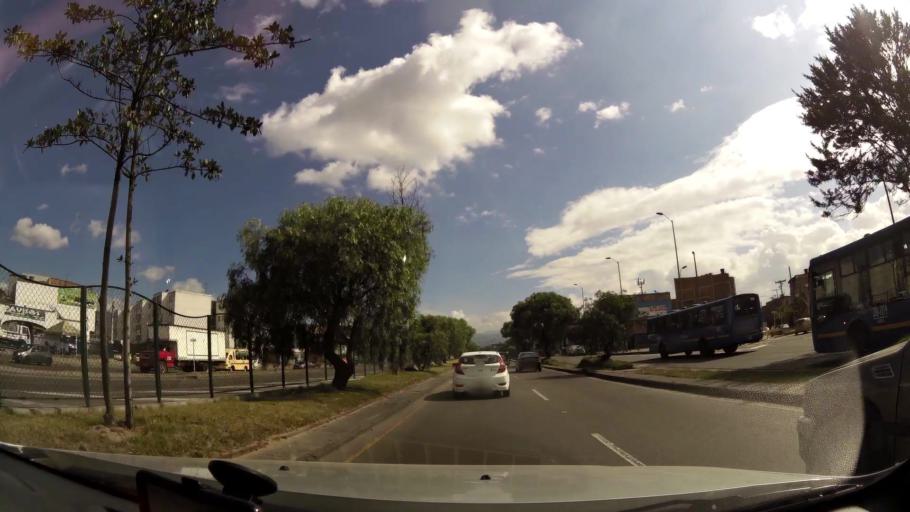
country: CO
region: Bogota D.C.
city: Bogota
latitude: 4.6176
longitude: -74.1398
